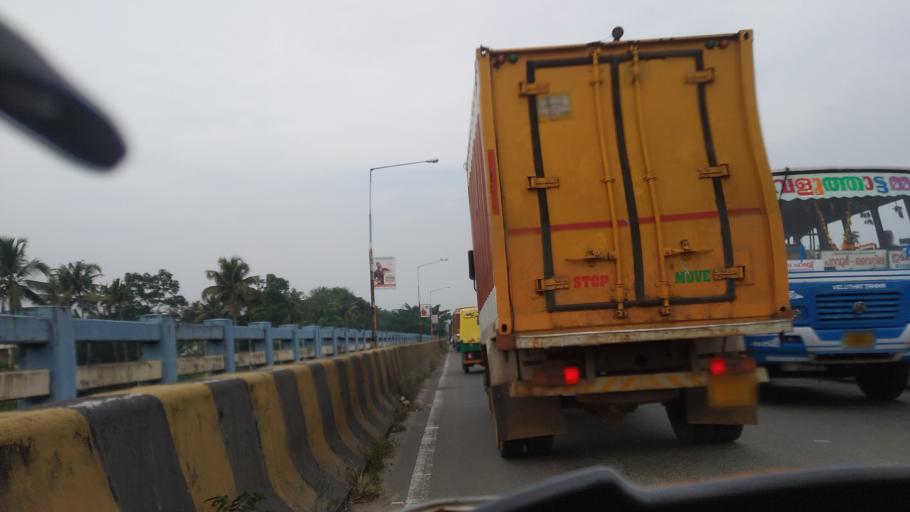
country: IN
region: Kerala
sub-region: Ernakulam
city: Elur
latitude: 10.0375
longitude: 76.3019
